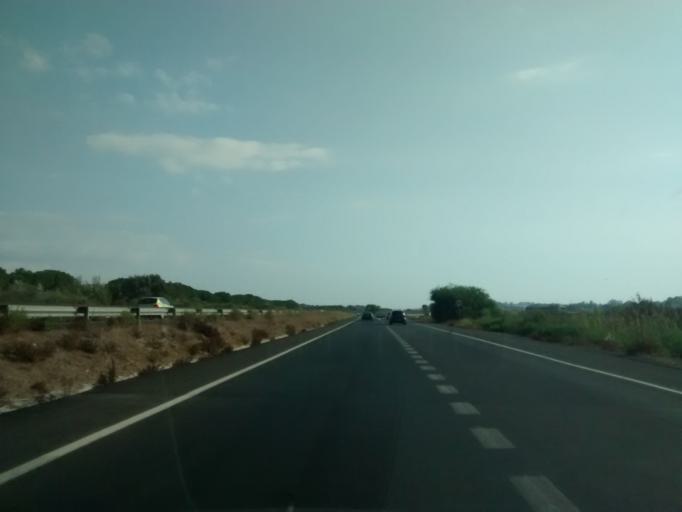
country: ES
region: Andalusia
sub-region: Provincia de Cadiz
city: Jerez de la Frontera
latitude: 36.7022
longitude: -6.0758
